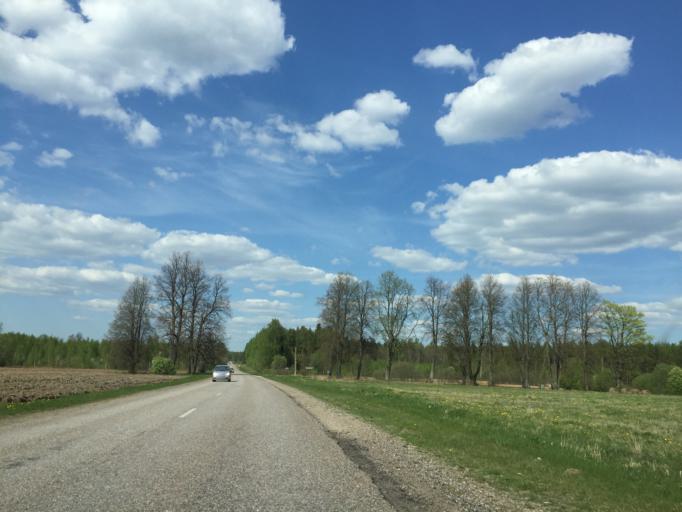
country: LV
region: Limbazu Rajons
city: Limbazi
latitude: 57.3886
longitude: 24.6891
